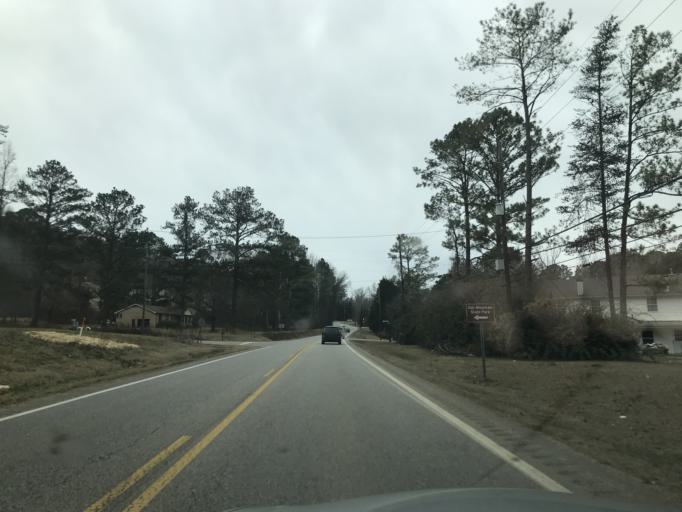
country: US
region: Alabama
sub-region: Shelby County
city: Meadowbrook
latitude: 33.3809
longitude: -86.7011
